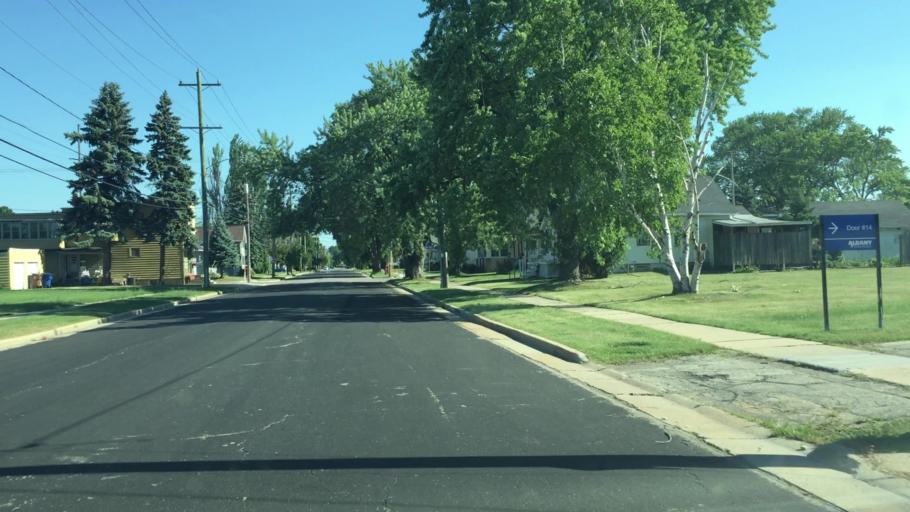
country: US
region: Wisconsin
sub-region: Winnebago County
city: Menasha
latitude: 44.2074
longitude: -88.4491
